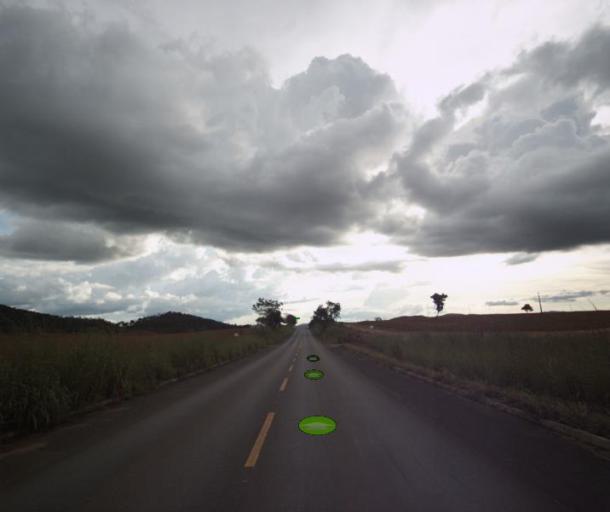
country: BR
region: Goias
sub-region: Niquelandia
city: Niquelandia
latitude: -14.5000
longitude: -48.5070
